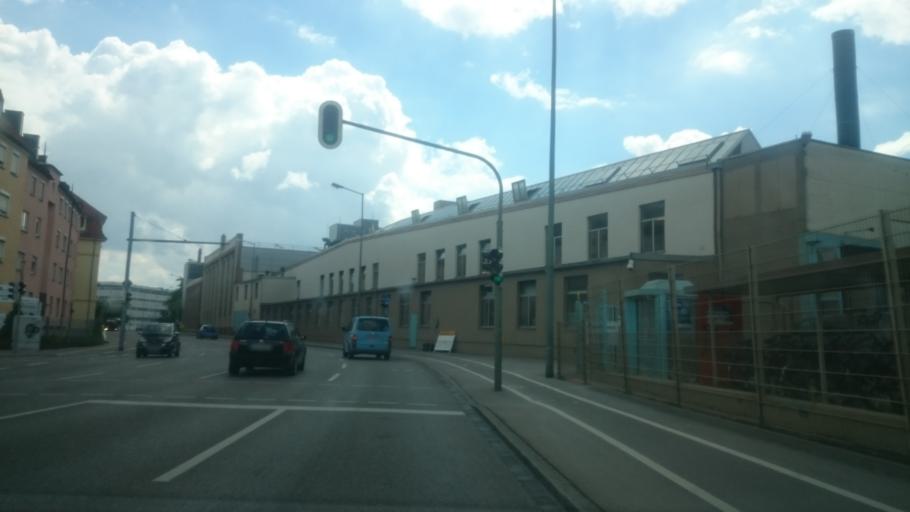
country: DE
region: Bavaria
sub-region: Swabia
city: Augsburg
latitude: 48.3837
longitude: 10.8896
